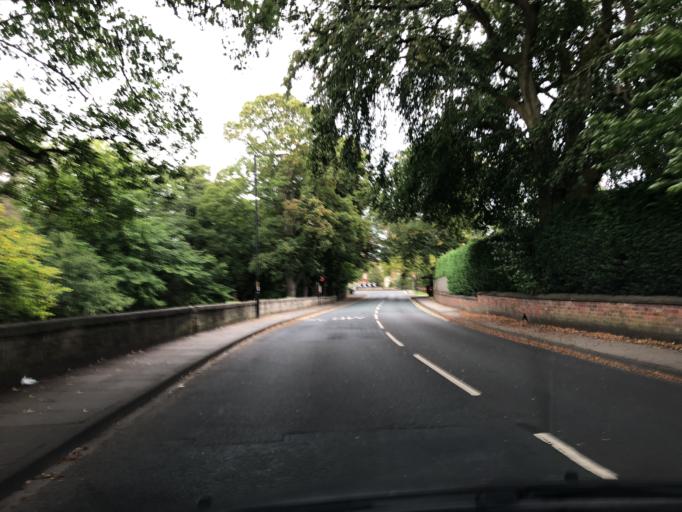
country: GB
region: England
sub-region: North Yorkshire
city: Ripon
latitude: 54.1326
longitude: -1.5273
